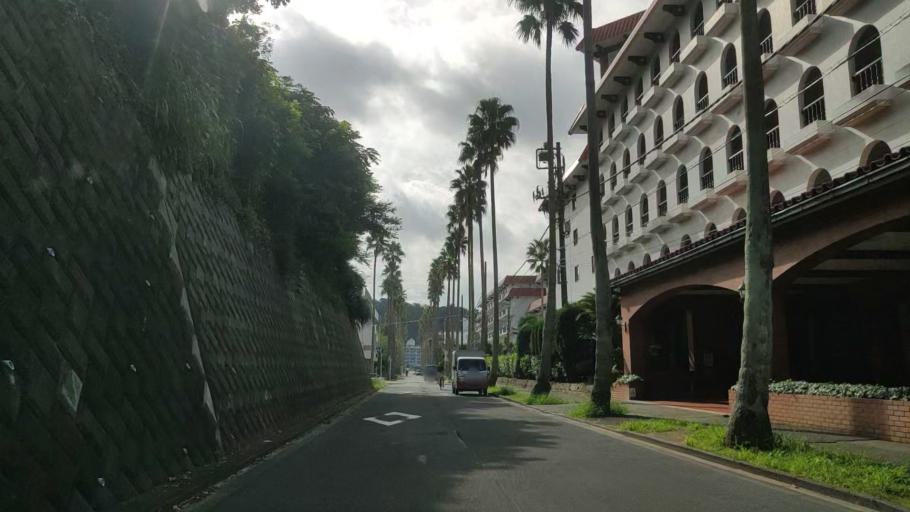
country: JP
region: Kanagawa
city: Kamakura
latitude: 35.2988
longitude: 139.5529
